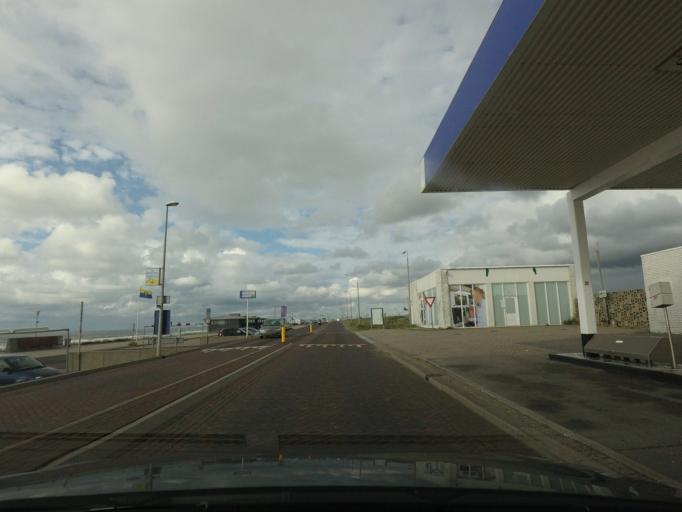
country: NL
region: North Holland
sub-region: Gemeente Zandvoort
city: Zandvoort
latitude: 52.3878
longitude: 4.5351
